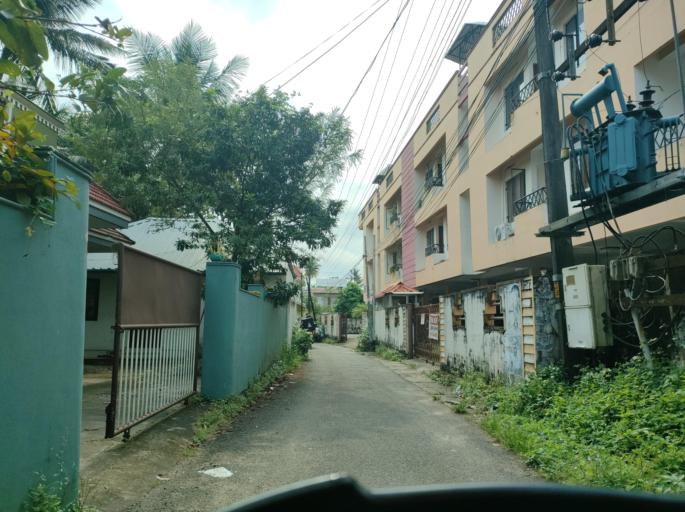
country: IN
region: Kerala
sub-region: Ernakulam
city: Elur
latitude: 9.9973
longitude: 76.3117
